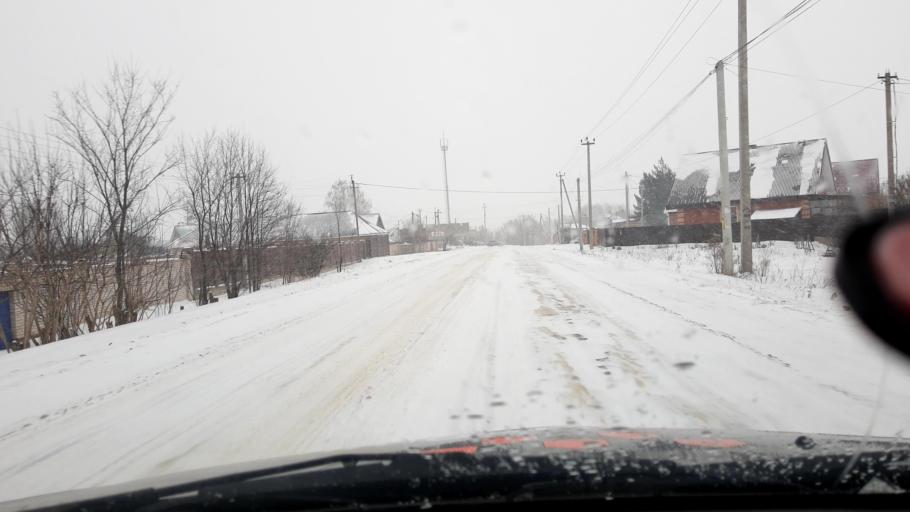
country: RU
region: Bashkortostan
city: Ufa
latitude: 54.5432
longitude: 55.9370
